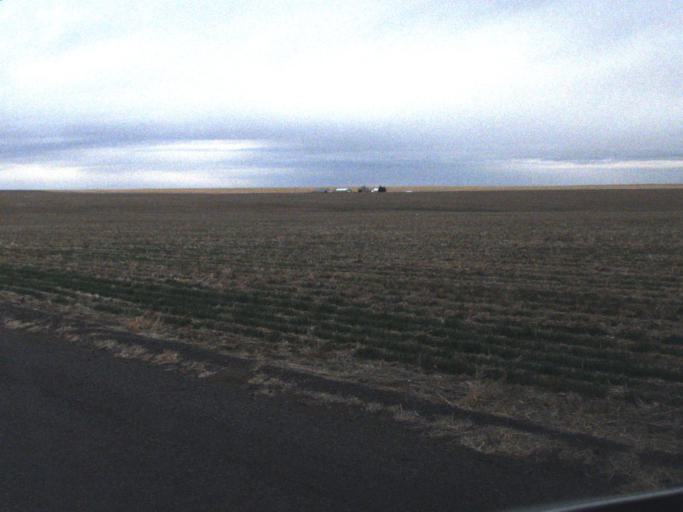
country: US
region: Washington
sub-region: Franklin County
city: Connell
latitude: 46.7945
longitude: -118.6331
